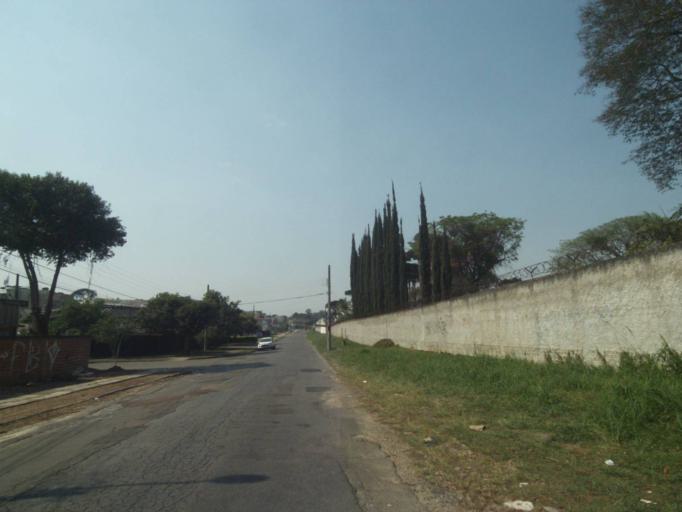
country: BR
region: Parana
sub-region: Sao Jose Dos Pinhais
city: Sao Jose dos Pinhais
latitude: -25.5179
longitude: -49.2507
